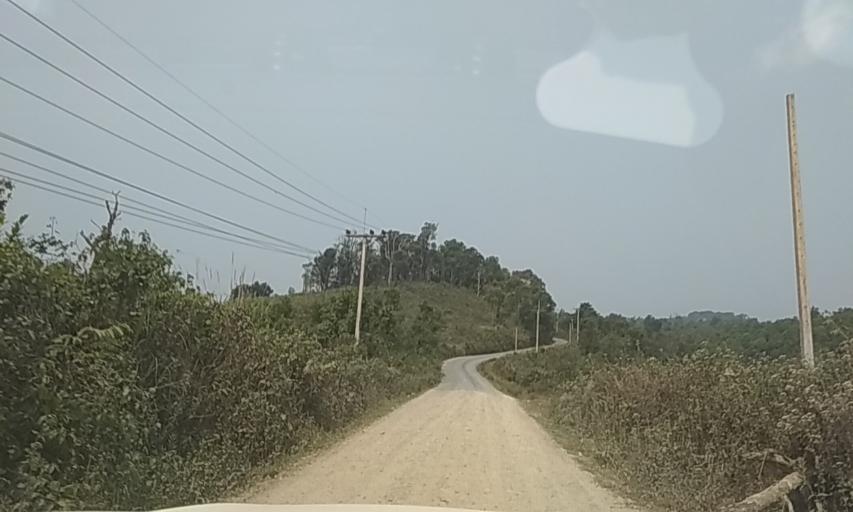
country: TH
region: Nan
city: Chaloem Phra Kiat
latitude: 20.0253
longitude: 101.0980
